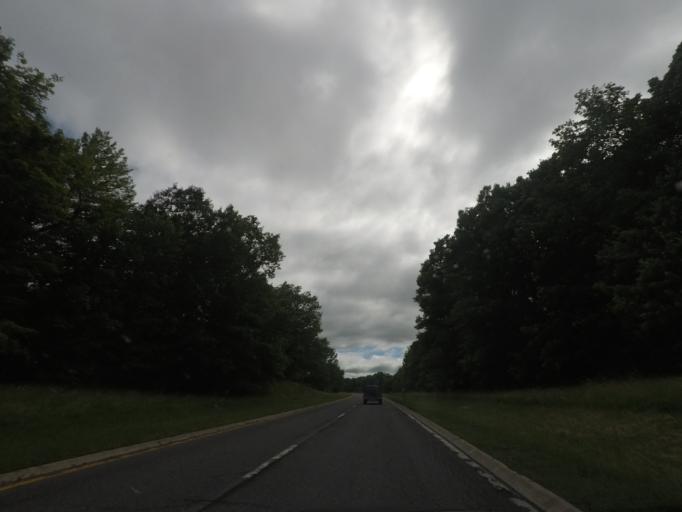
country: US
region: New York
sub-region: Columbia County
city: Philmont
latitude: 42.2785
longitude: -73.6097
